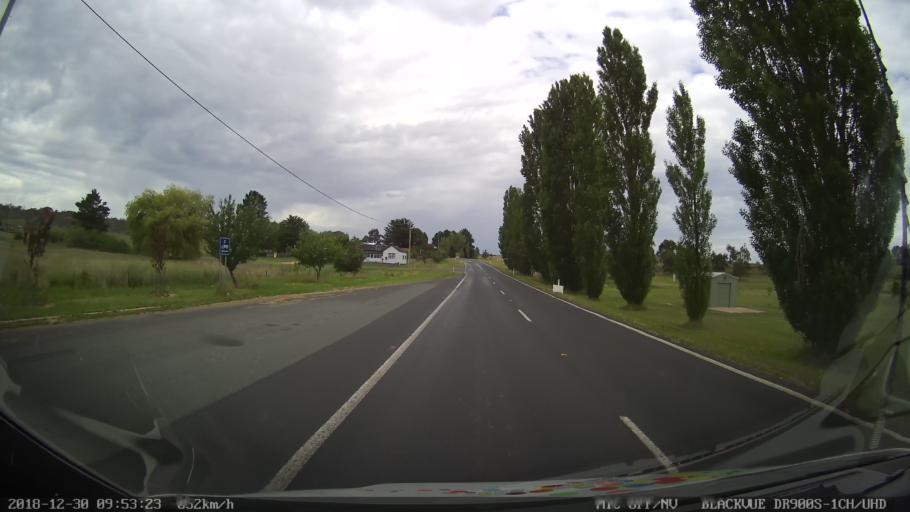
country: AU
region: New South Wales
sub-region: Cooma-Monaro
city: Cooma
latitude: -36.5154
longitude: 149.2825
